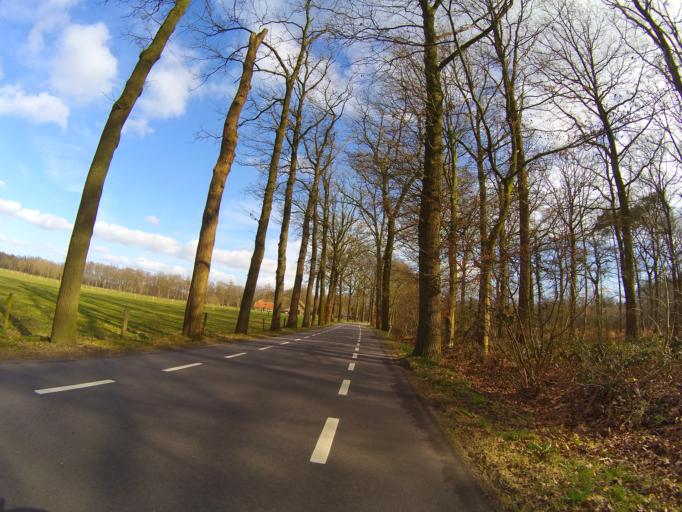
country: NL
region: Gelderland
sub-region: Gemeente Barneveld
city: Terschuur
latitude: 52.1495
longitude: 5.5371
